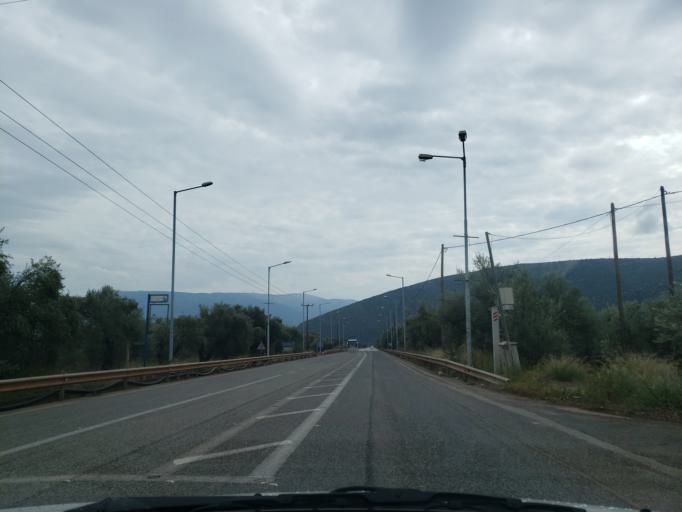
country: GR
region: Central Greece
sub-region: Nomos Fokidos
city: Amfissa
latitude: 38.4924
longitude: 22.4146
